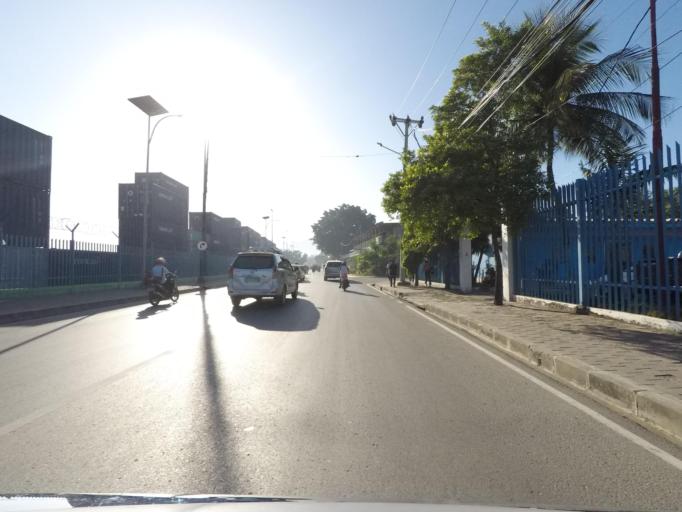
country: TL
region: Dili
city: Dili
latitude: -8.5541
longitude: 125.5752
